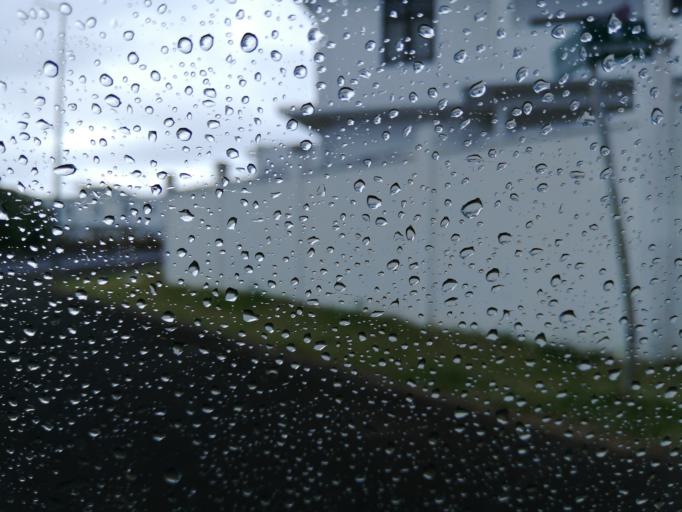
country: MU
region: Plaines Wilhems
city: Ebene
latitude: -20.2457
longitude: 57.4831
